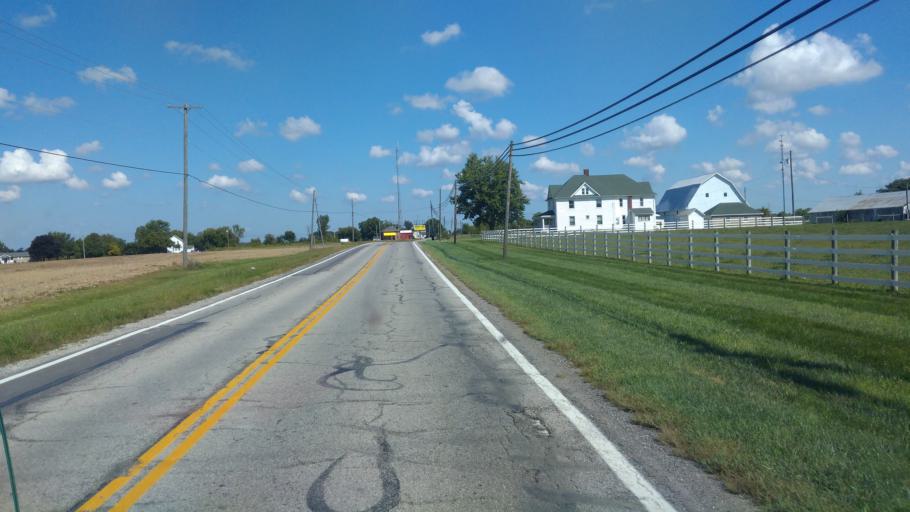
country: US
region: Ohio
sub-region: Marion County
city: Marion
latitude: 40.6241
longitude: -83.1307
